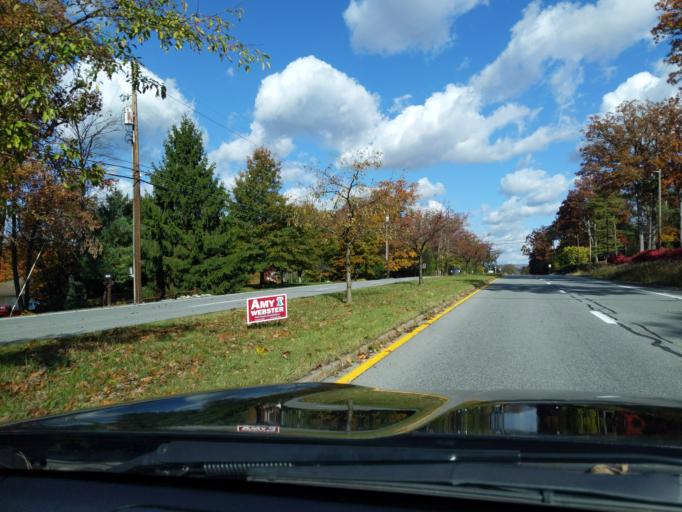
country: US
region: Pennsylvania
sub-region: Blair County
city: Hollidaysburg
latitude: 40.4441
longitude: -78.3929
